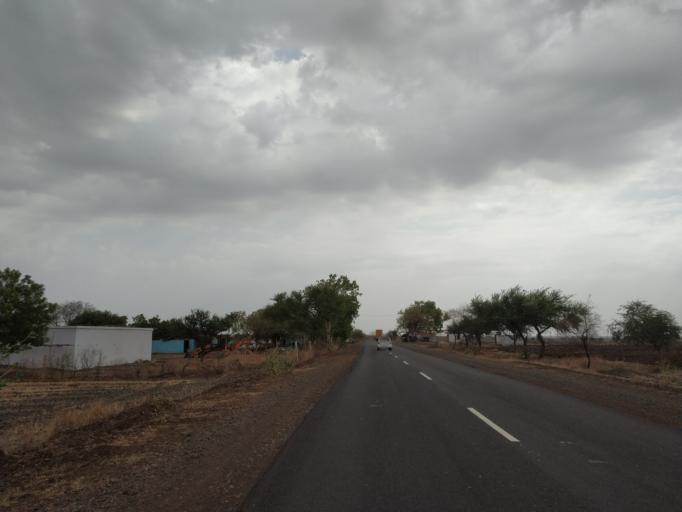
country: IN
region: Madhya Pradesh
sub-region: Shajapur
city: Susner
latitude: 24.0341
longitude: 76.1410
